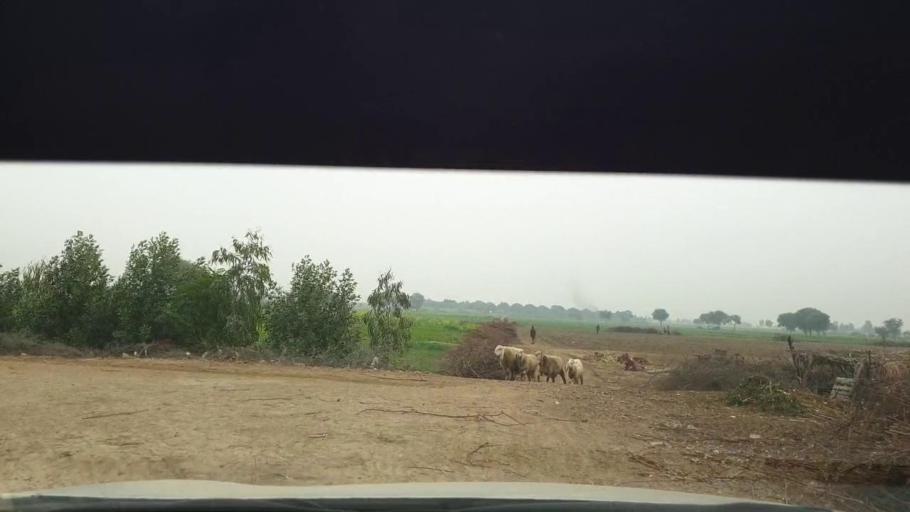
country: PK
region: Sindh
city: Berani
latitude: 25.7573
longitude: 68.7405
